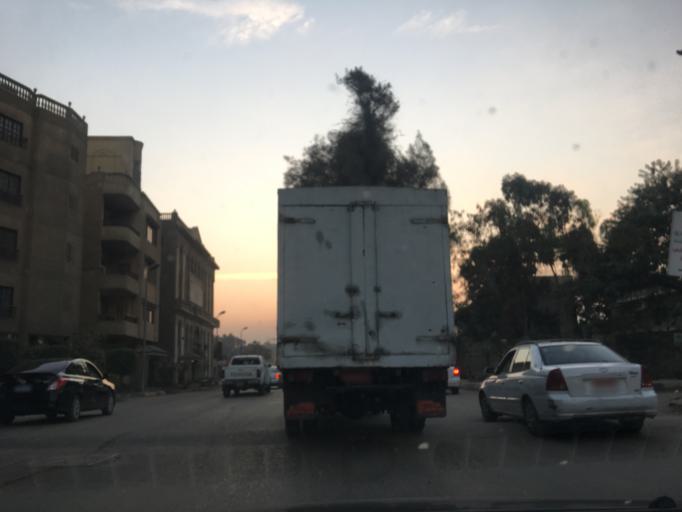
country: EG
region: Al Jizah
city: Al Jizah
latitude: 29.9919
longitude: 31.1284
